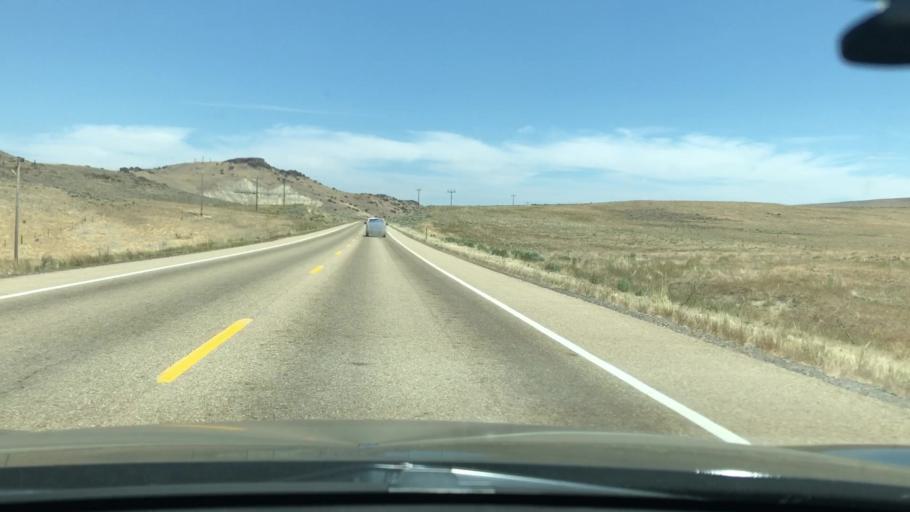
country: US
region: Idaho
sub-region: Owyhee County
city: Marsing
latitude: 43.3427
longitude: -116.9521
